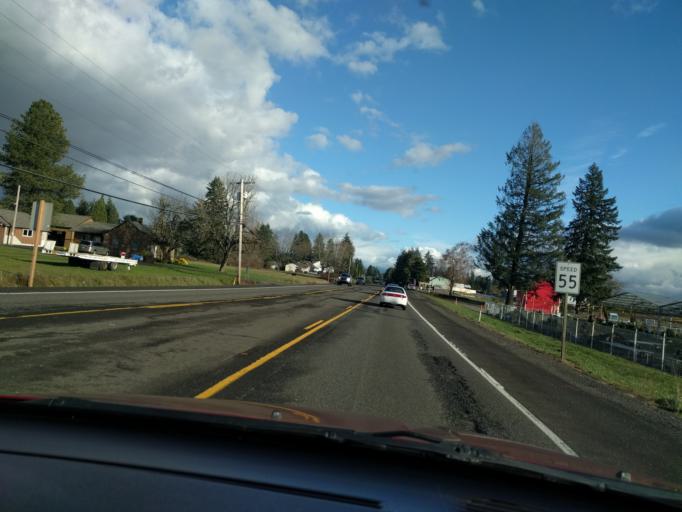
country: US
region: Oregon
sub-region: Clackamas County
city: Damascus
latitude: 45.4180
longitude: -122.4191
